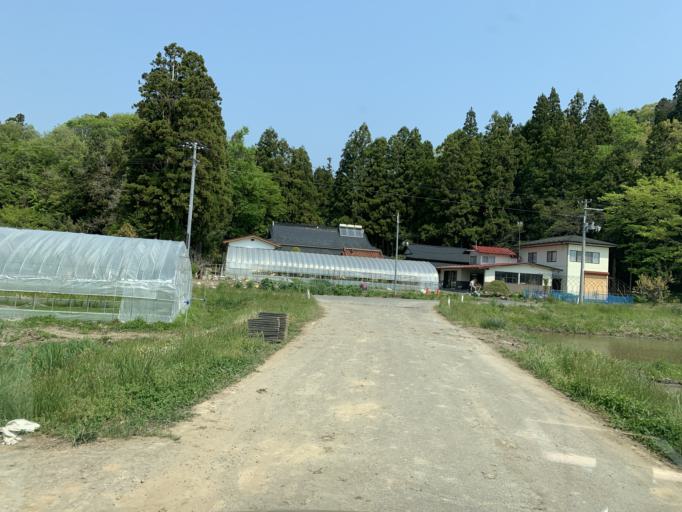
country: JP
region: Iwate
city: Ichinoseki
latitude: 38.8621
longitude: 141.0569
